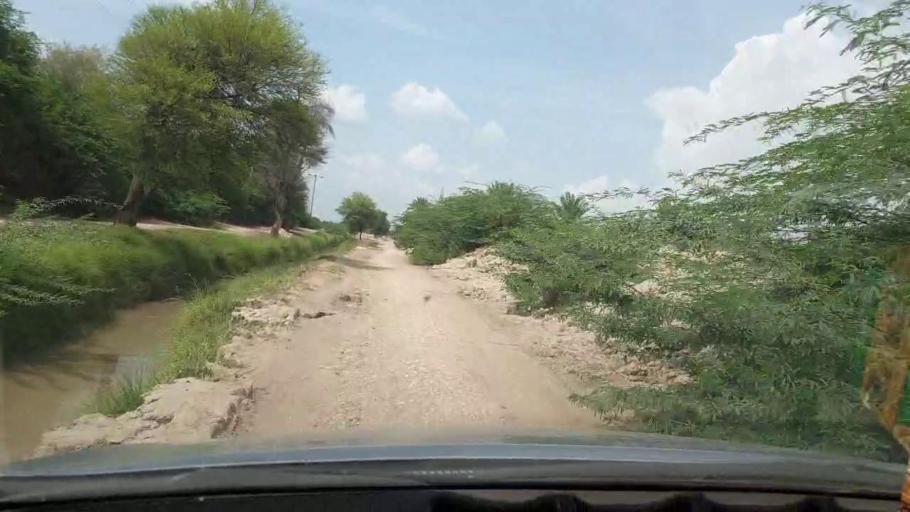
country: PK
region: Sindh
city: Khairpur
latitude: 27.4767
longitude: 68.8508
